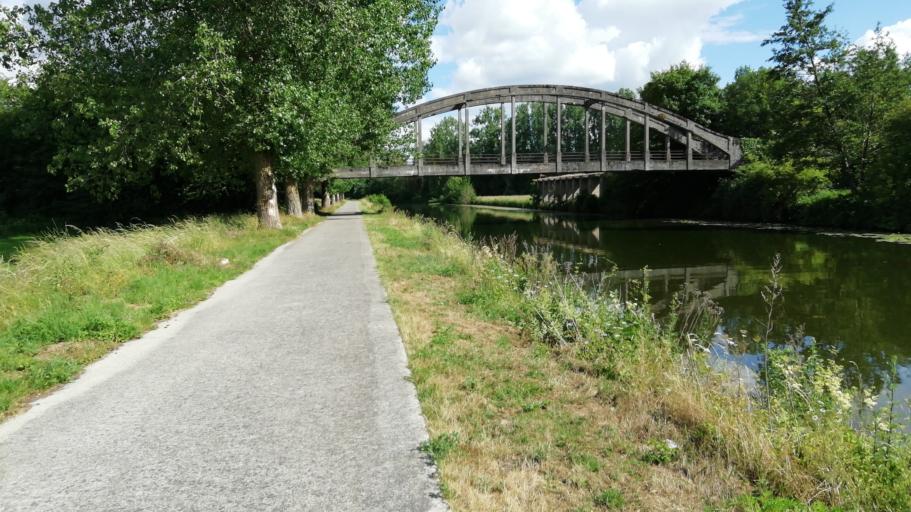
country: BE
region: Wallonia
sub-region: Province du Hainaut
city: Merbes-le-Chateau
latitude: 50.3210
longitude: 4.1664
